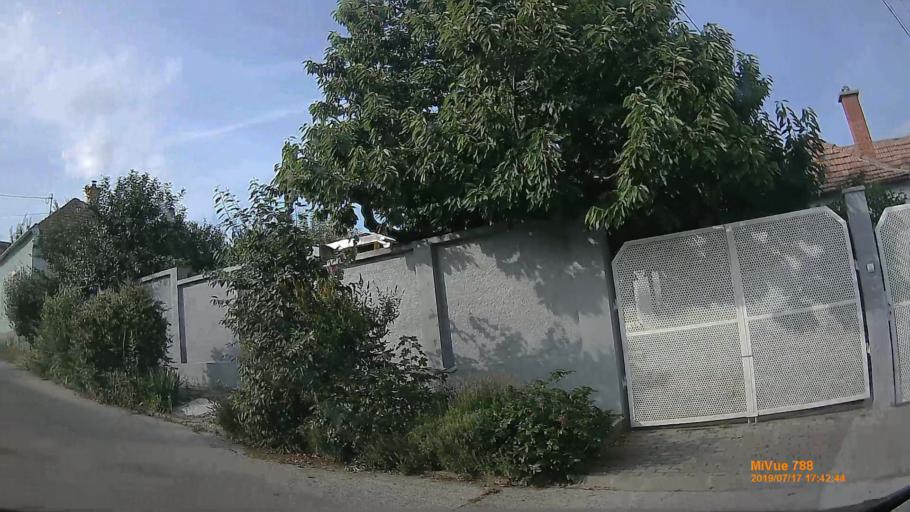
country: HU
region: Veszprem
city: Ajka
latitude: 47.1083
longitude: 17.5703
